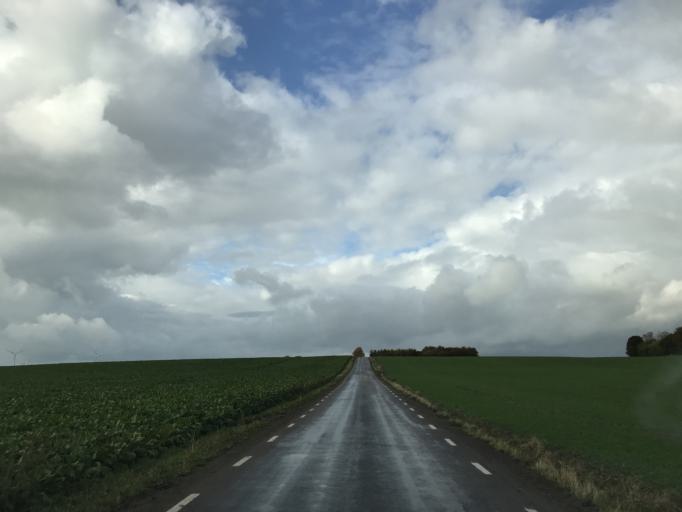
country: SE
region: Skane
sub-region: Svalovs Kommun
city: Svaloev
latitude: 55.9046
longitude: 13.1749
